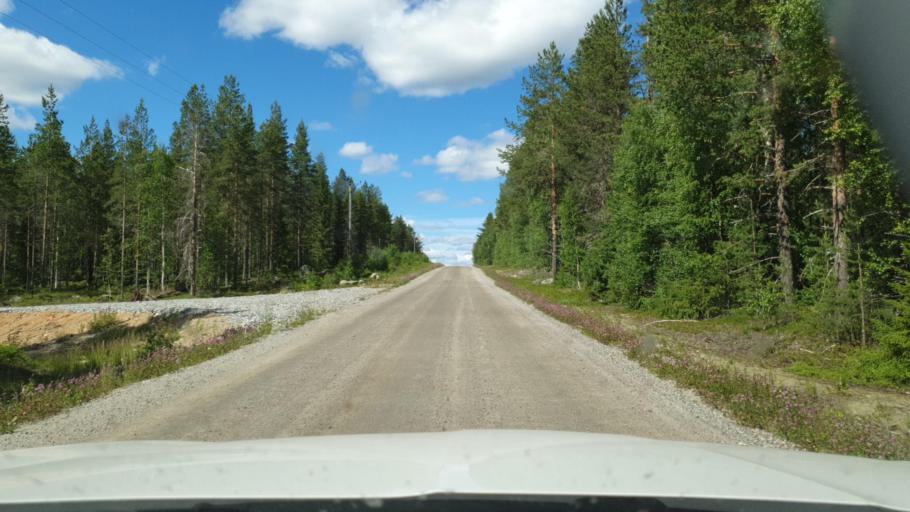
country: SE
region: Norrbotten
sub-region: Pitea Kommun
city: Roknas
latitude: 65.1614
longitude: 21.1488
